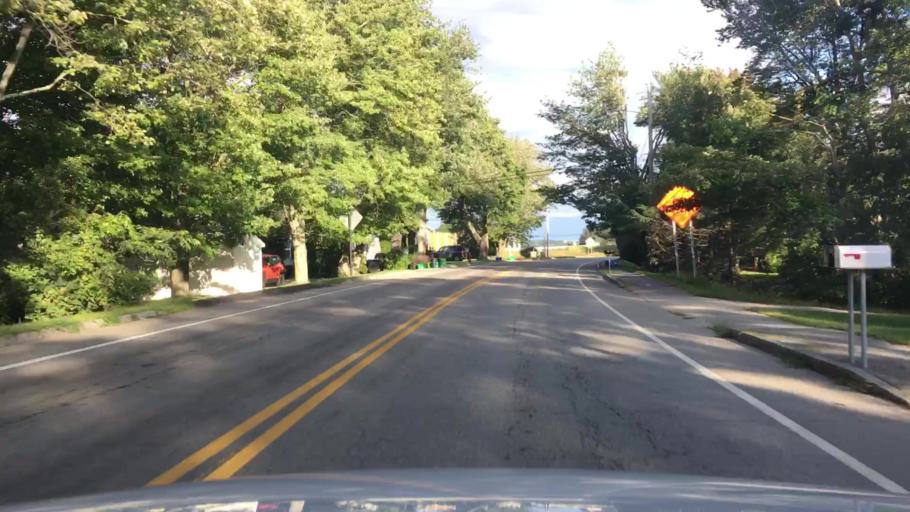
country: US
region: Maine
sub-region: York County
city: Eliot
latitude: 43.1277
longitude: -70.8420
